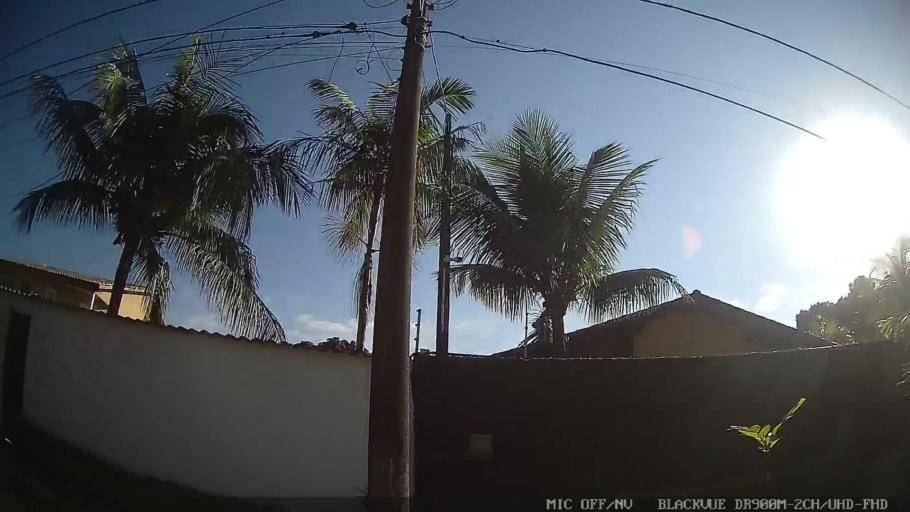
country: BR
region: Sao Paulo
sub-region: Guaruja
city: Guaruja
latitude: -24.0152
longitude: -46.2811
